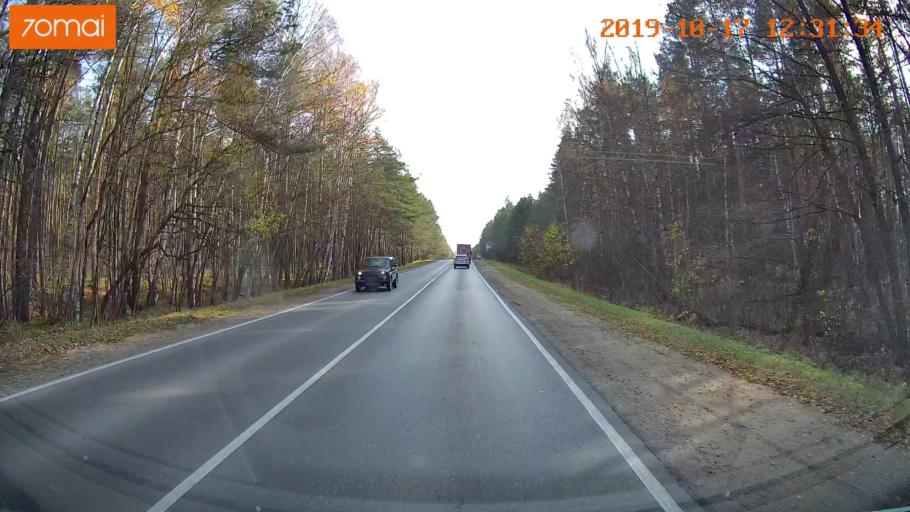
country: RU
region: Rjazan
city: Syntul
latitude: 54.9671
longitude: 41.3354
